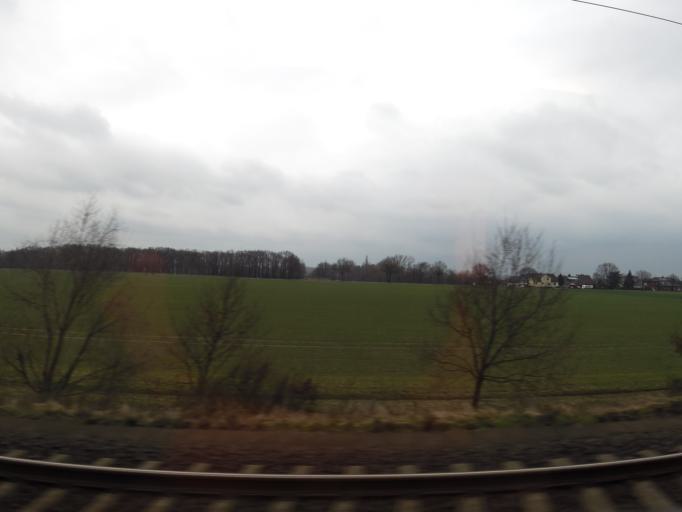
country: DE
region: Lower Saxony
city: Garbsen
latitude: 52.4014
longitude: 9.5468
